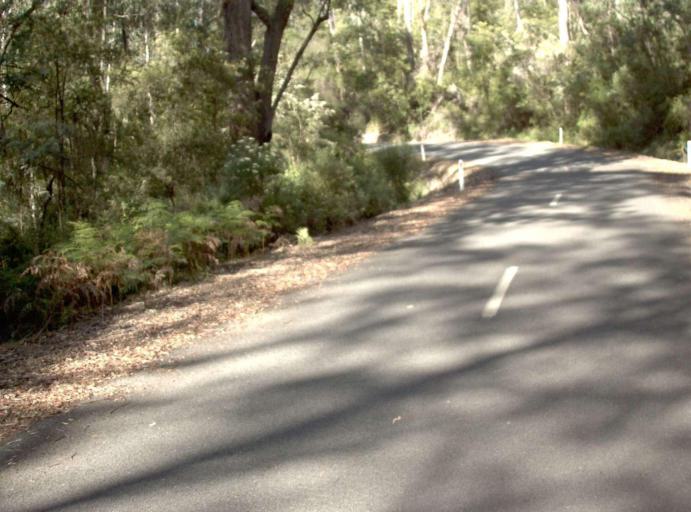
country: AU
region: Victoria
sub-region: East Gippsland
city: Lakes Entrance
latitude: -37.5030
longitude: 148.5429
